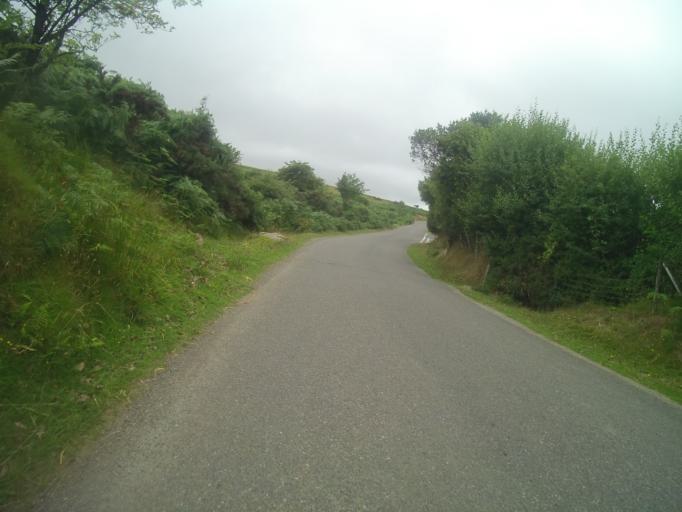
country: GB
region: England
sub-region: Devon
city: Buckfastleigh
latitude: 50.5162
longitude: -3.8428
